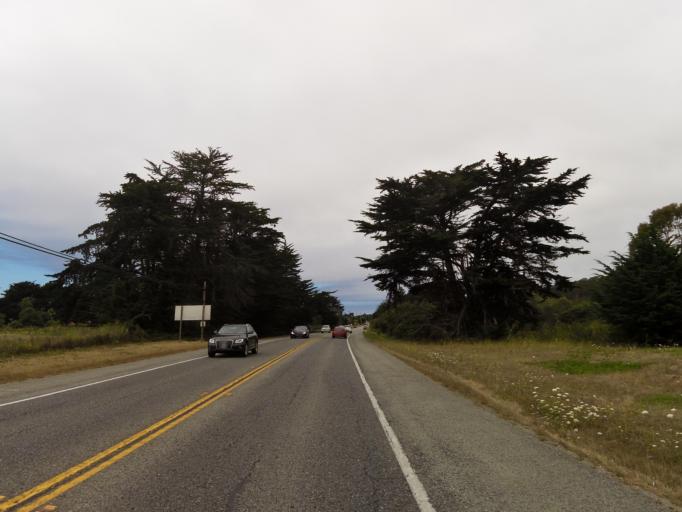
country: US
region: California
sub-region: San Mateo County
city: Moss Beach
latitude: 37.5219
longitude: -122.5076
